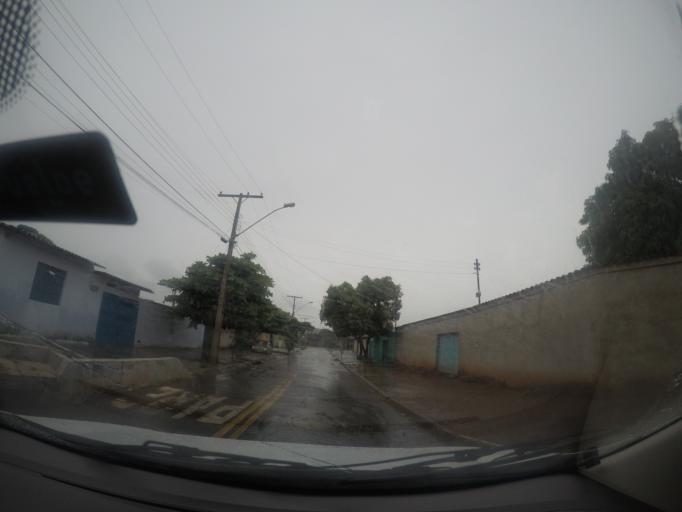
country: BR
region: Goias
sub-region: Goiania
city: Goiania
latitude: -16.6546
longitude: -49.3117
